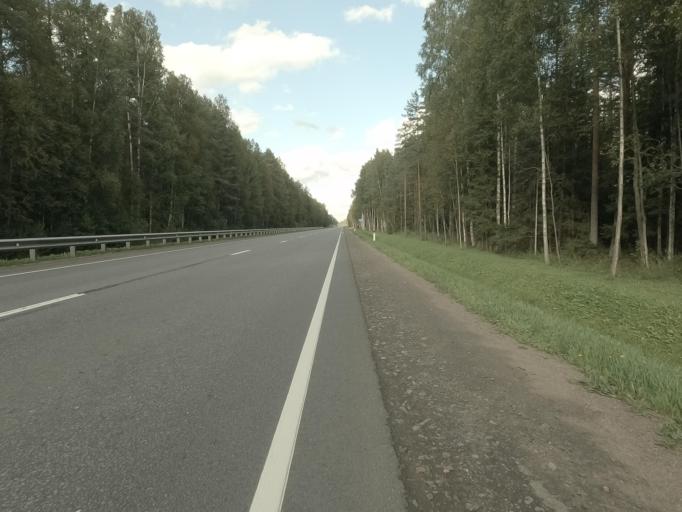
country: RU
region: Leningrad
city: Mga
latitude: 59.7028
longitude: 31.0043
